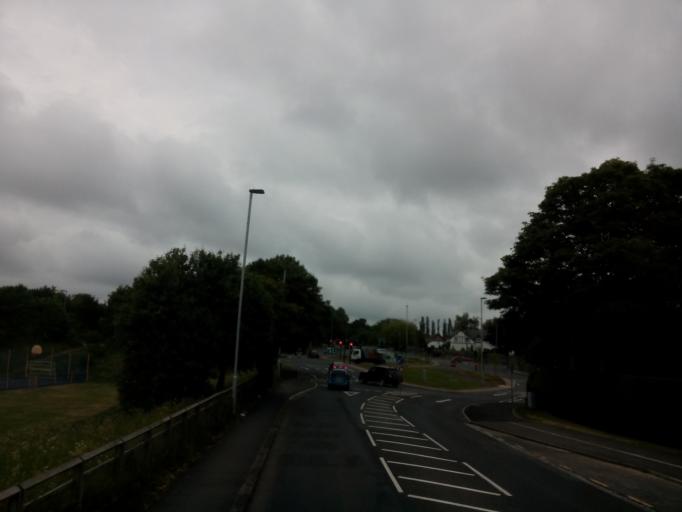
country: GB
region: England
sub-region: County Durham
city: Chester-le-Street
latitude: 54.8665
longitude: -1.5749
